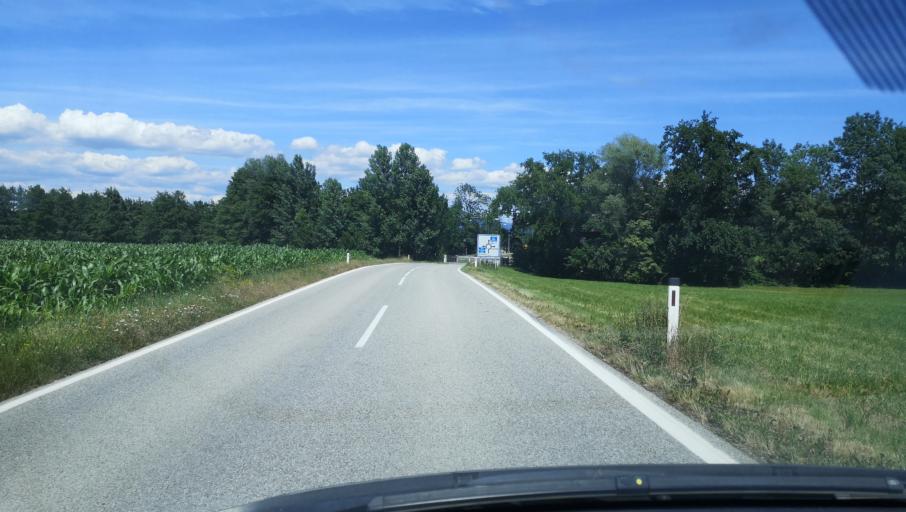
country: AT
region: Lower Austria
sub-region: Politischer Bezirk Amstetten
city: Euratsfeld
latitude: 48.0921
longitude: 14.9248
